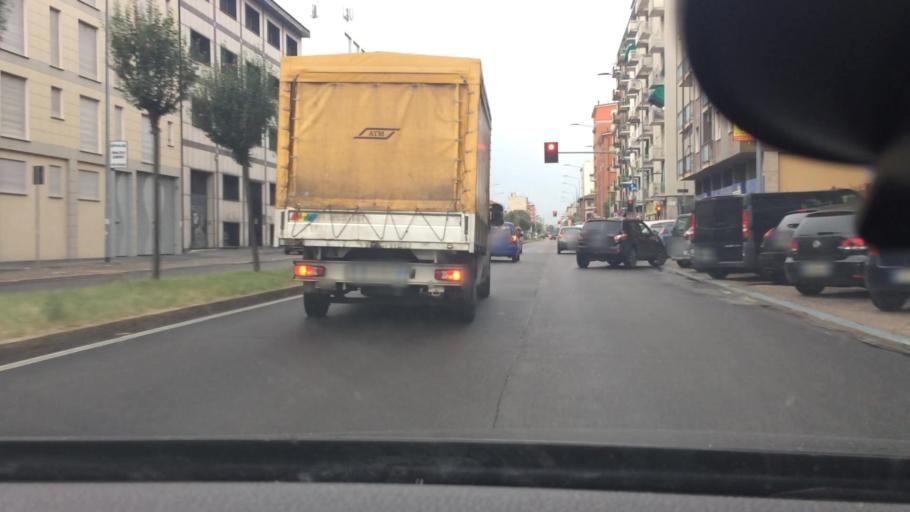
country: IT
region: Lombardy
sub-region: Citta metropolitana di Milano
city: Sesto San Giovanni
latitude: 45.5105
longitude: 9.2241
